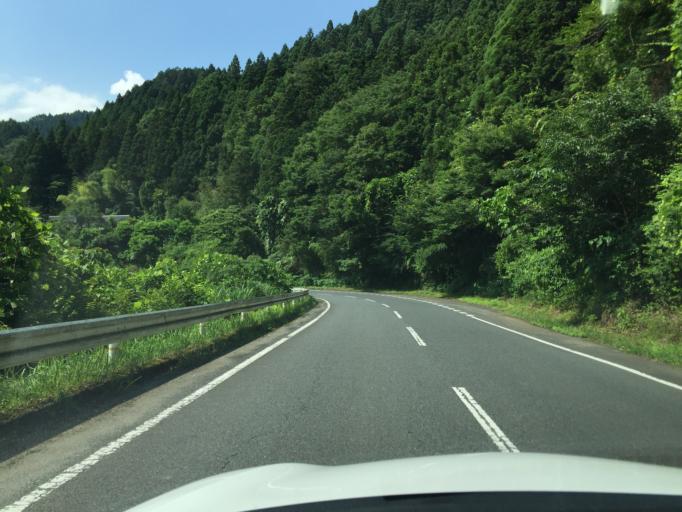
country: JP
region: Ibaraki
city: Kitaibaraki
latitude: 36.9469
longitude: 140.7161
